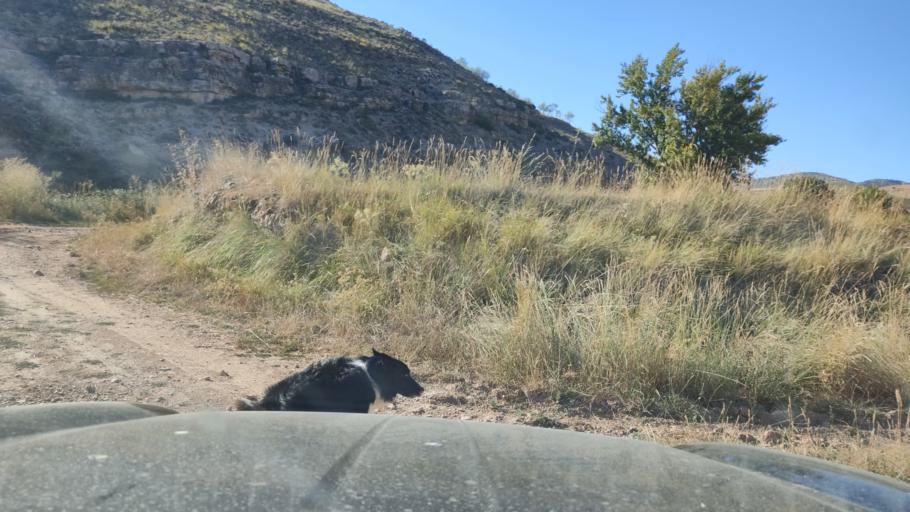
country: ES
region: Aragon
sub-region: Provincia de Teruel
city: Monforte de Moyuela
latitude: 41.0455
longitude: -1.0135
